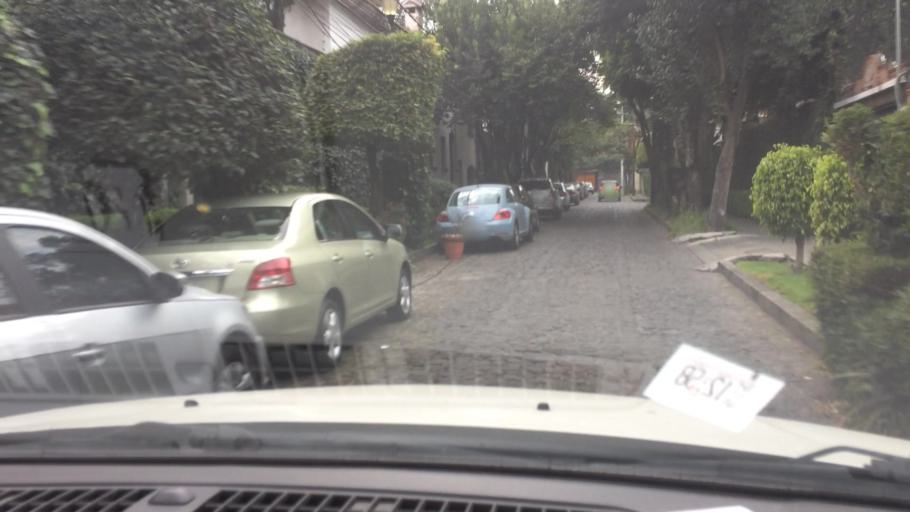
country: MX
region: Mexico City
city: Alvaro Obregon
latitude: 19.3523
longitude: -99.1921
